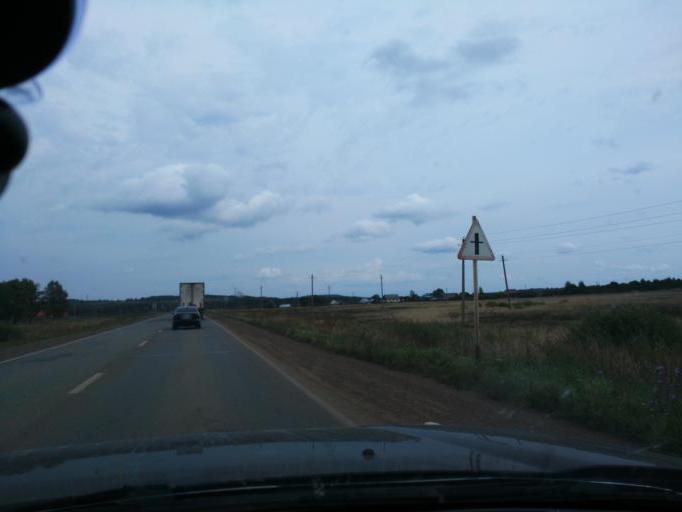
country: RU
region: Perm
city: Kuyeda
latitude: 56.4506
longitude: 55.6069
